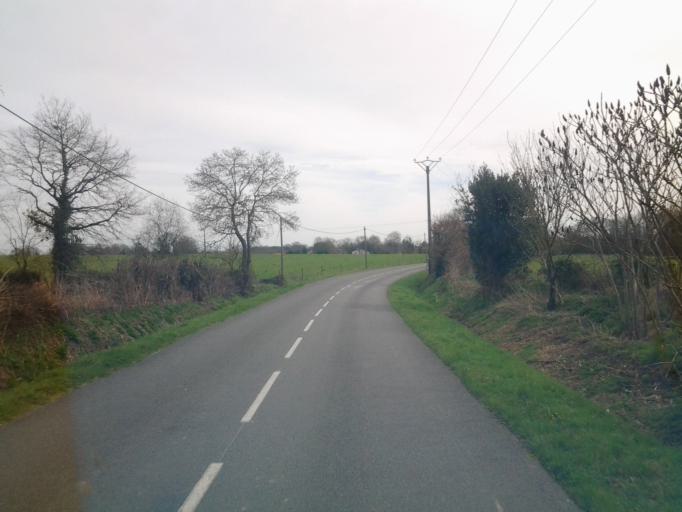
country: FR
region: Pays de la Loire
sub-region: Departement de la Vendee
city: Venansault
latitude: 46.6871
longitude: -1.5336
